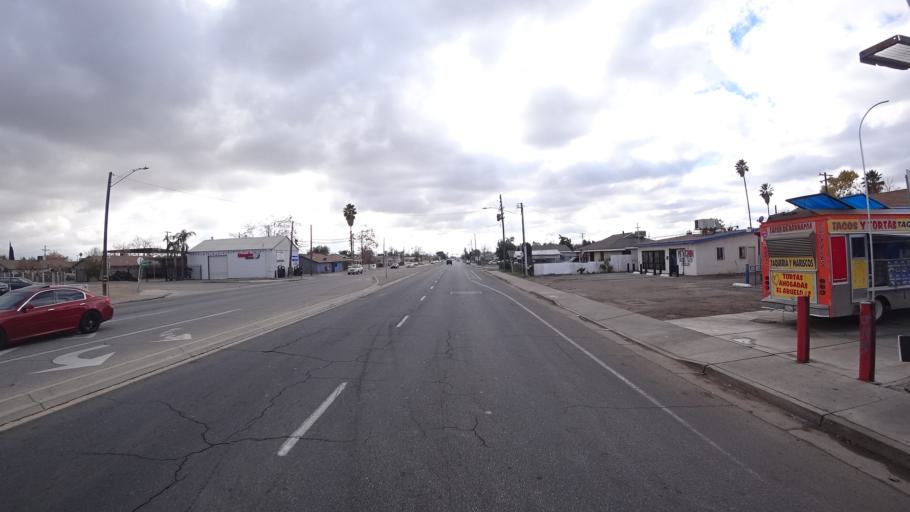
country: US
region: California
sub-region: Kern County
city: Bakersfield
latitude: 35.3680
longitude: -118.9676
